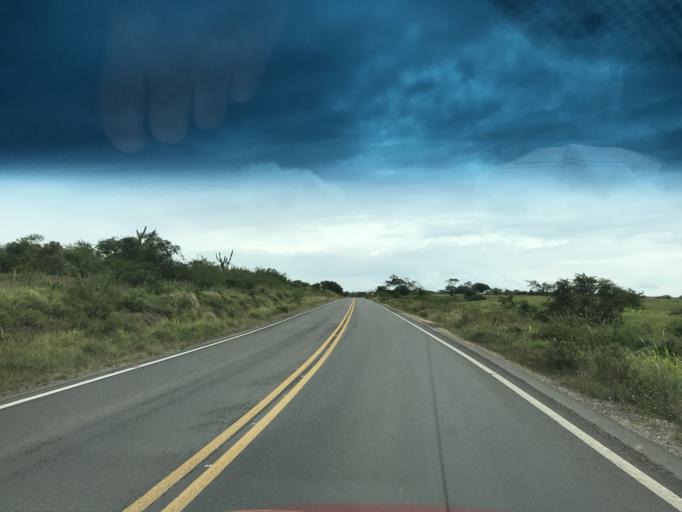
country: BR
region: Bahia
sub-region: Castro Alves
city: Castro Alves
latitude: -12.7530
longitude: -39.4074
